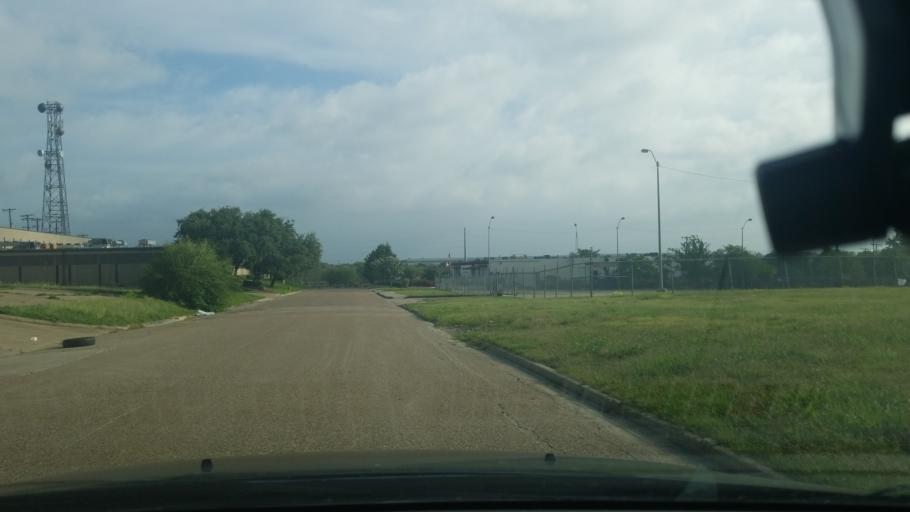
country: US
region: Texas
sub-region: Dallas County
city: Mesquite
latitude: 32.7724
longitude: -96.6451
